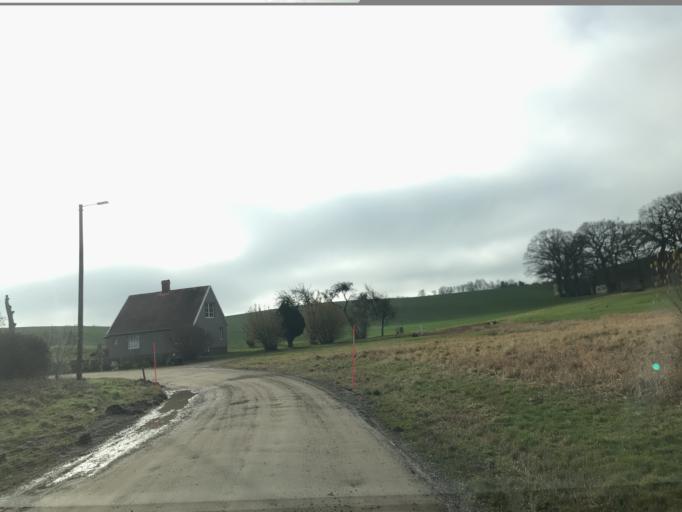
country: SE
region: Skane
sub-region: Svalovs Kommun
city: Teckomatorp
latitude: 55.8346
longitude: 13.0663
